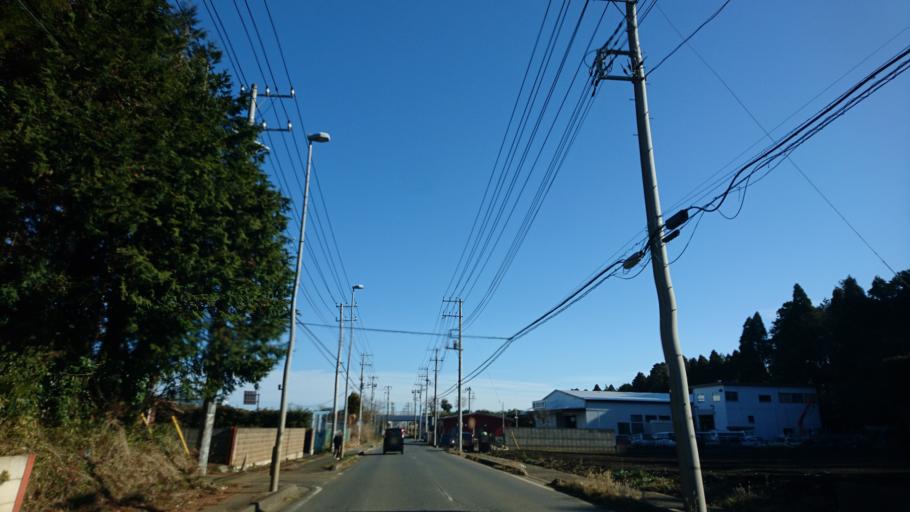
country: JP
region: Chiba
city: Togane
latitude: 35.5843
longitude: 140.3128
